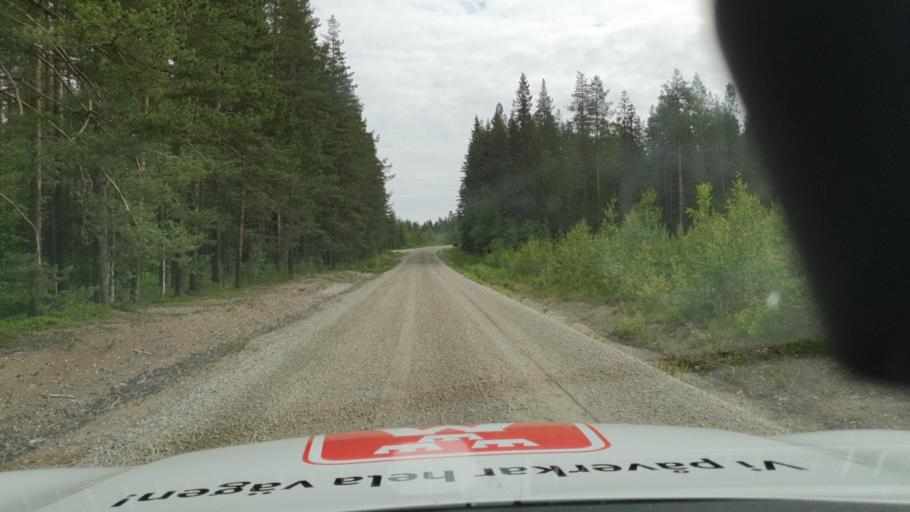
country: SE
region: Vaesterbotten
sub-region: Skelleftea Kommun
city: Forsbacka
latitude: 64.6551
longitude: 20.4330
